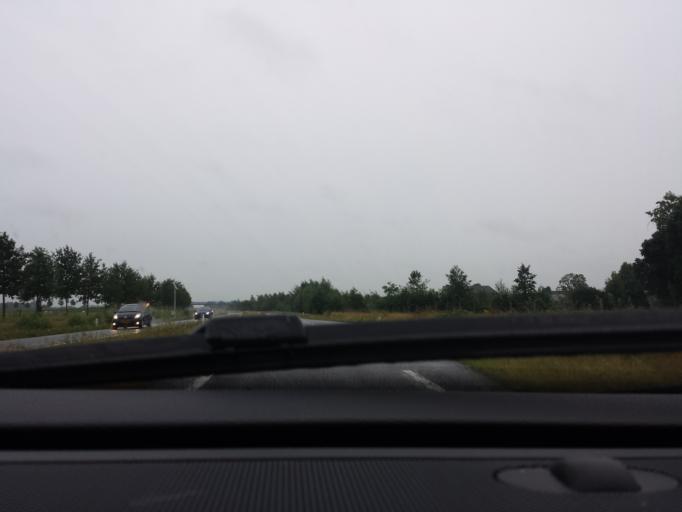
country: NL
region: Gelderland
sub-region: Gemeente Montferland
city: s-Heerenberg
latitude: 51.9082
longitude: 6.2682
